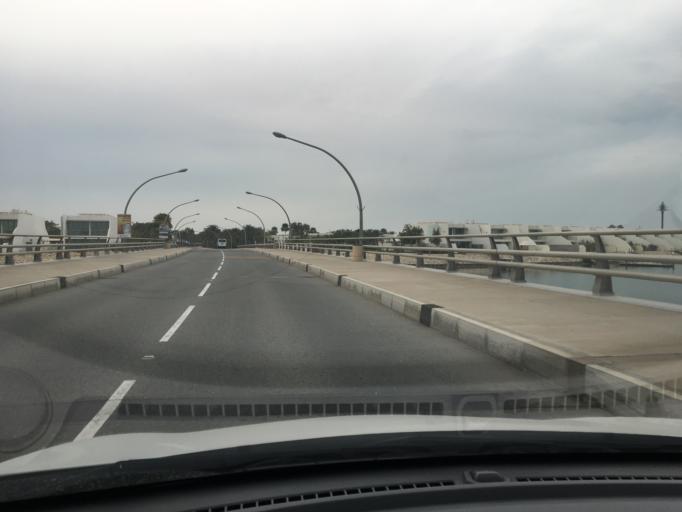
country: BH
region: Central Governorate
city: Dar Kulayb
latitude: 25.8422
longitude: 50.6142
